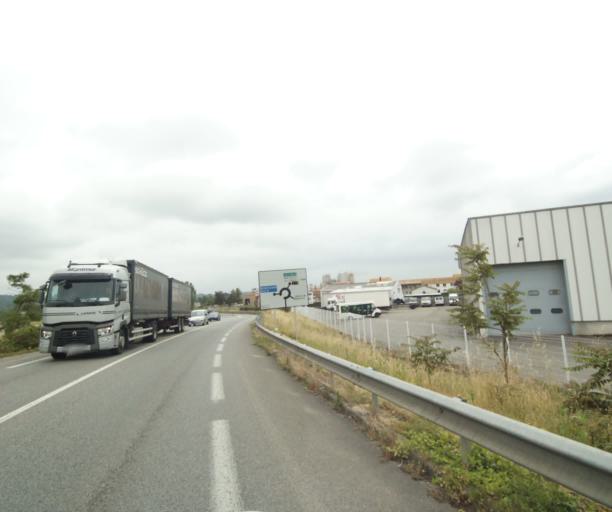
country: FR
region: Midi-Pyrenees
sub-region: Departement du Tarn-et-Garonne
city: Bressols
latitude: 43.9779
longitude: 1.3354
